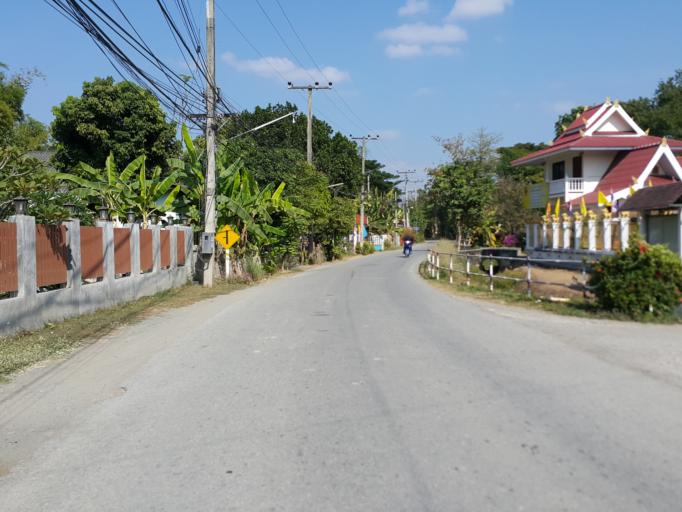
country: TH
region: Chiang Mai
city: San Kamphaeng
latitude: 18.8127
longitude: 99.1546
